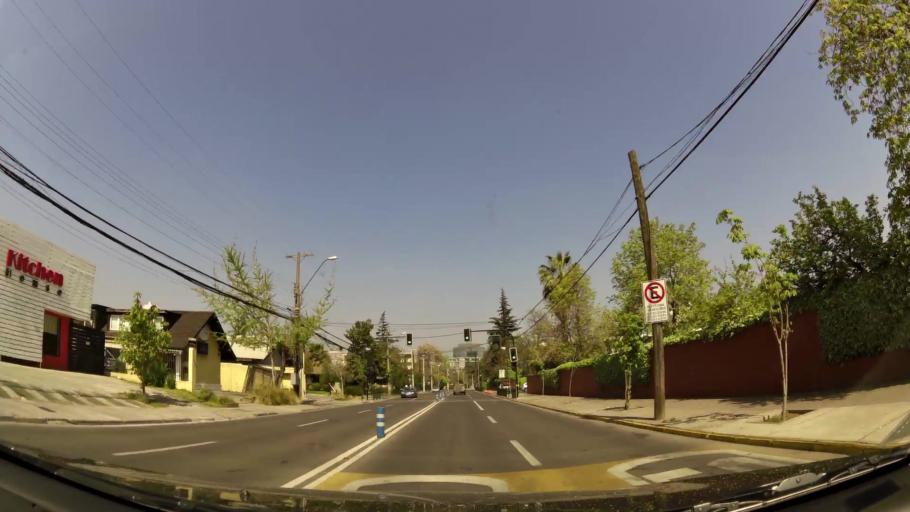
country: CL
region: Santiago Metropolitan
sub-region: Provincia de Santiago
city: Villa Presidente Frei, Nunoa, Santiago, Chile
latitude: -33.3944
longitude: -70.5818
